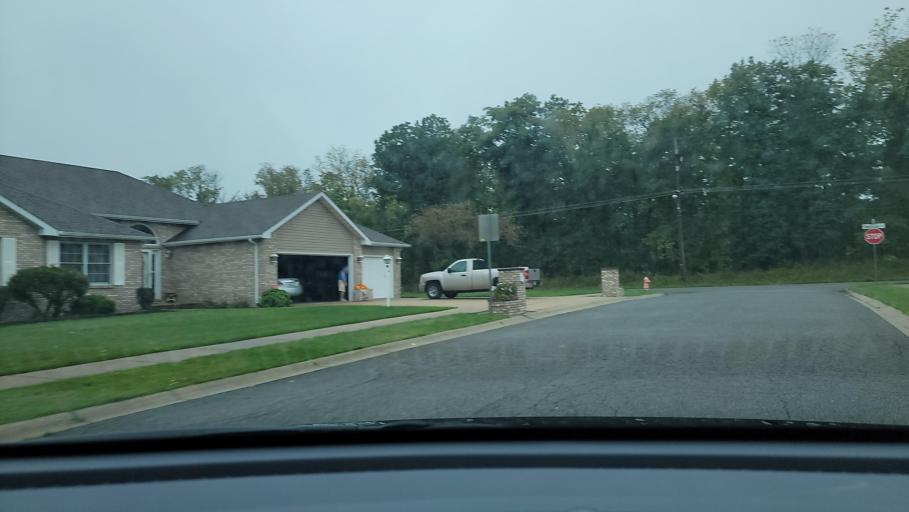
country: US
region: Indiana
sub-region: Porter County
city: Portage
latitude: 41.5394
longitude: -87.1963
